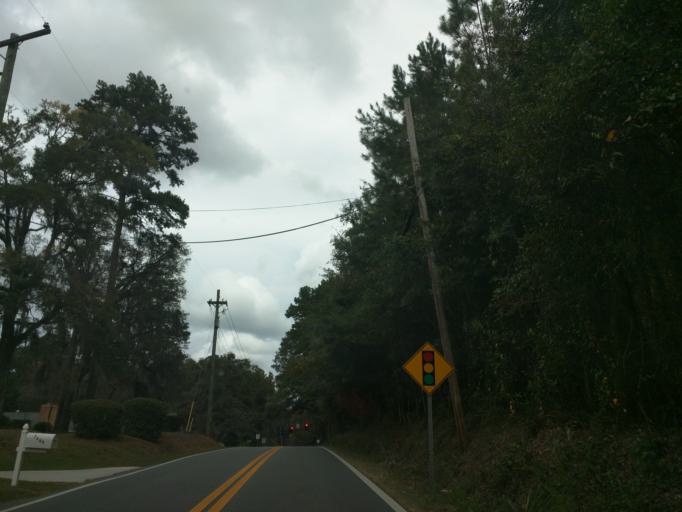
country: US
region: Florida
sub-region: Leon County
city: Tallahassee
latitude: 30.4138
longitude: -84.2098
